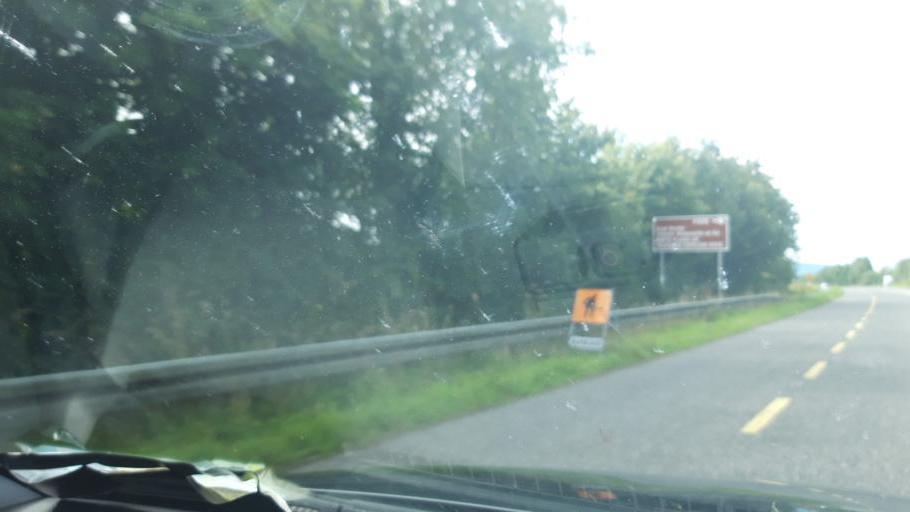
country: IE
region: Leinster
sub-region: Kilkenny
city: Callan
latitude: 52.5515
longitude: -7.3883
